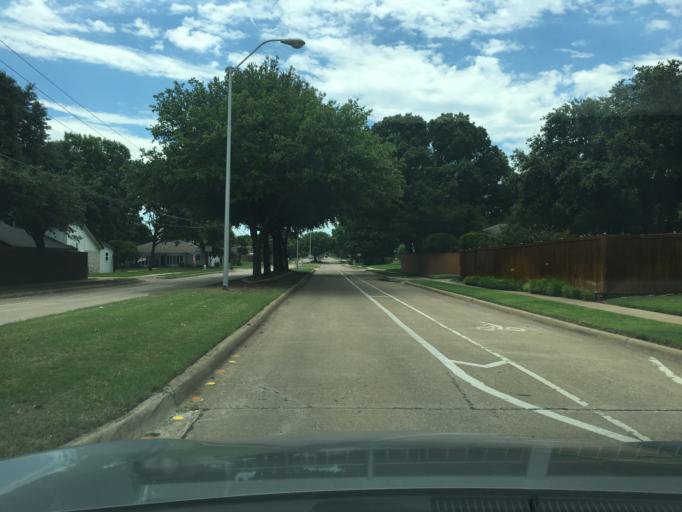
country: US
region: Texas
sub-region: Dallas County
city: Richardson
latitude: 32.9504
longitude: -96.6914
